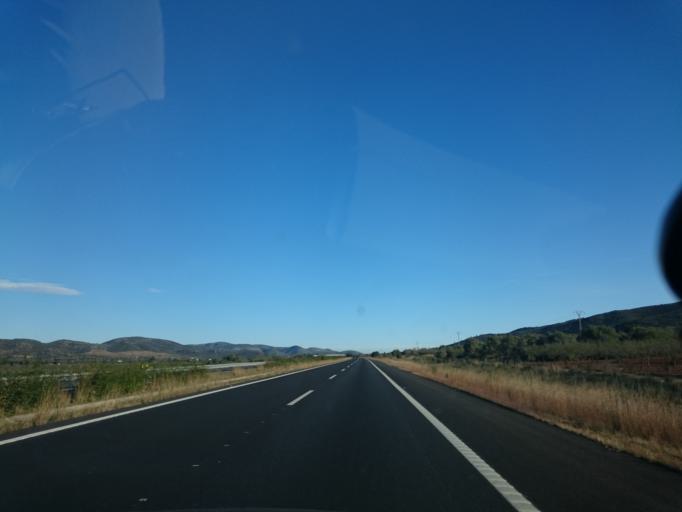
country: ES
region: Valencia
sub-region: Provincia de Castello
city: Alcala de Xivert
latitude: 40.3144
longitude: 0.2461
